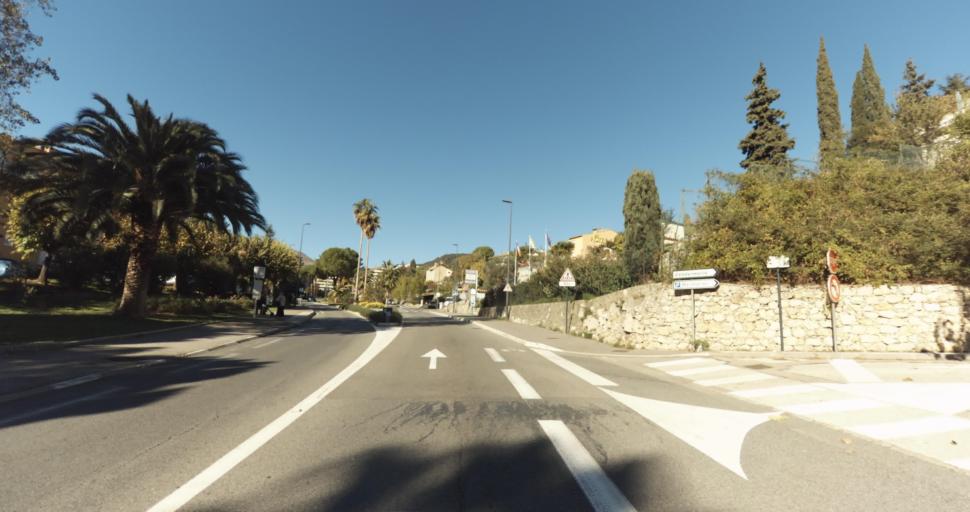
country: FR
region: Provence-Alpes-Cote d'Azur
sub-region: Departement des Alpes-Maritimes
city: Vence
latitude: 43.7193
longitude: 7.1134
